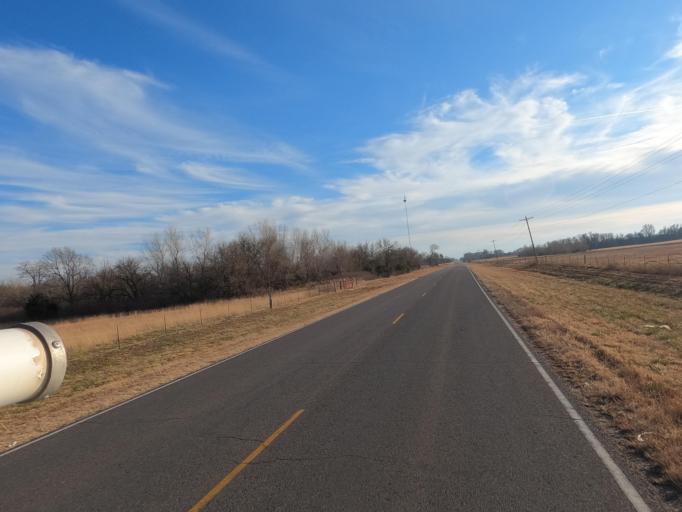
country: US
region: Kansas
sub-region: Reno County
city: Buhler
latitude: 38.1042
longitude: -97.7756
